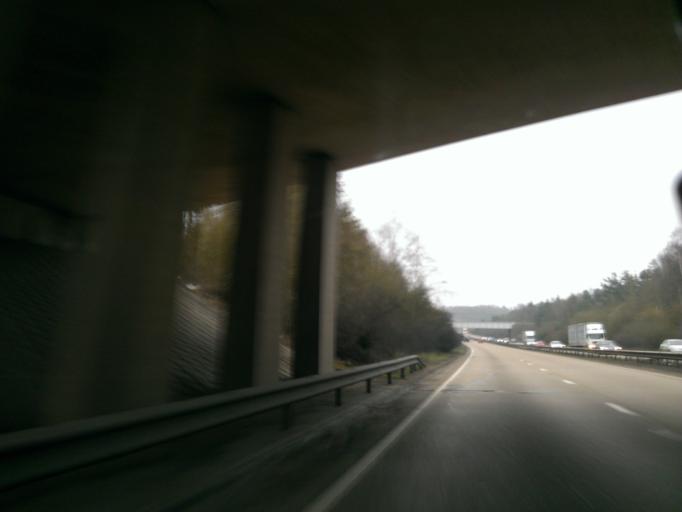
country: GB
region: England
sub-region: Essex
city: Colchester
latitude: 51.9127
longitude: 0.9522
